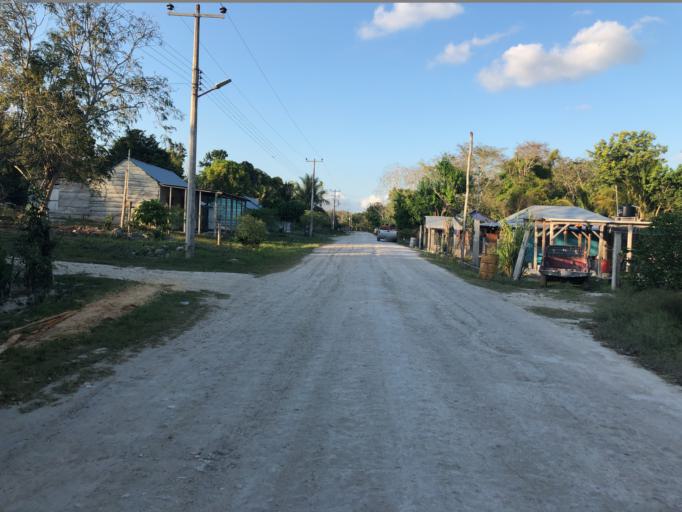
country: MX
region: Quintana Roo
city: Nicolas Bravo
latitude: 18.4528
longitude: -89.3064
